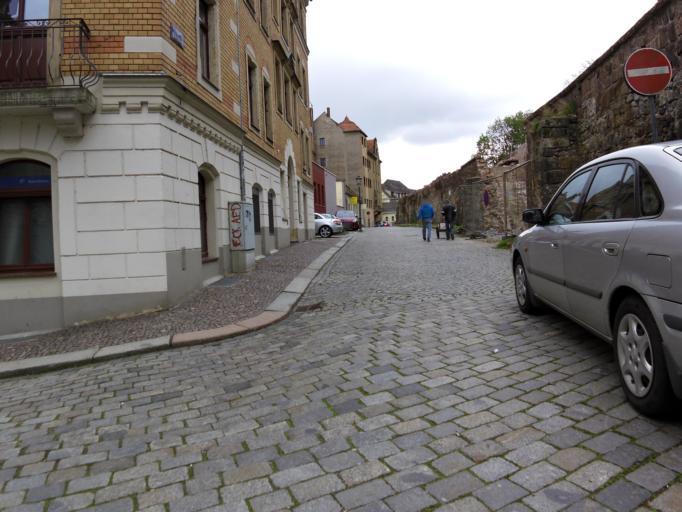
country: DE
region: Saxony
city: Meissen
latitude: 51.1599
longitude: 13.4697
